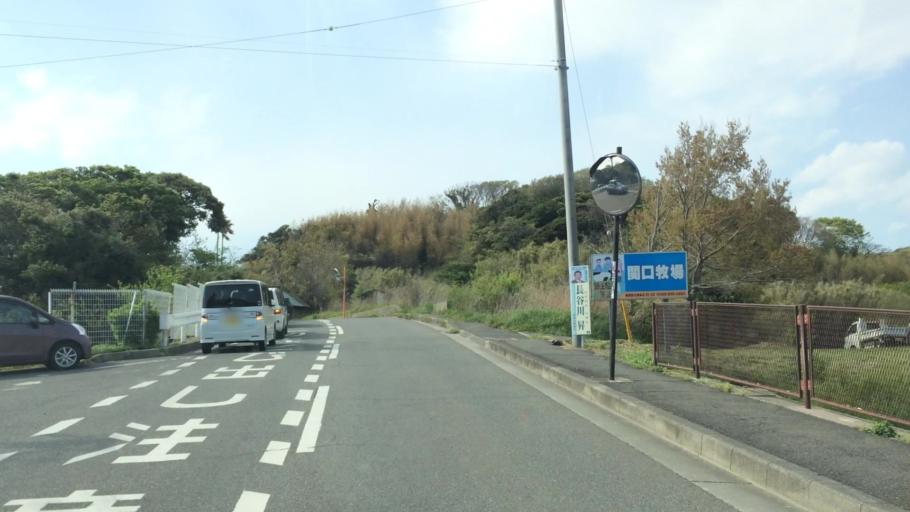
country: JP
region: Kanagawa
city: Yokosuka
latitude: 35.2322
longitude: 139.6298
